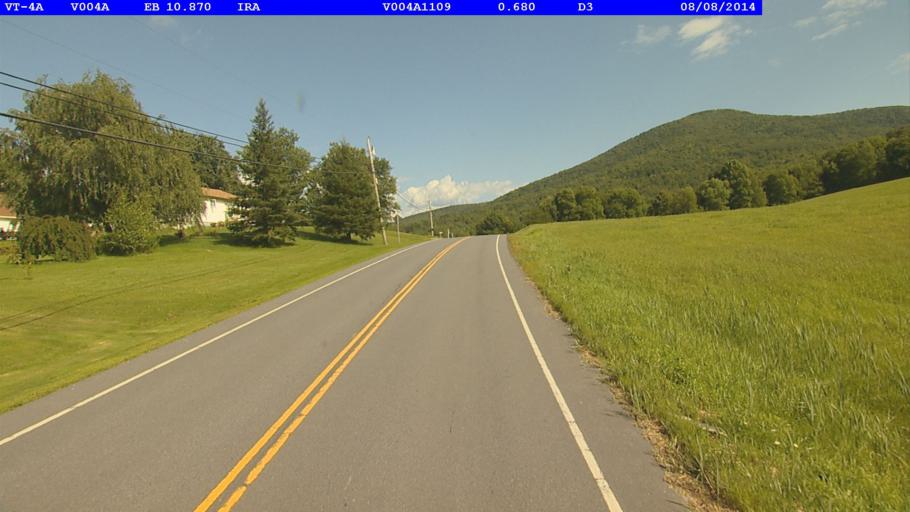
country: US
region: Vermont
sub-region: Rutland County
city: West Rutland
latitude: 43.6092
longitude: -73.0998
